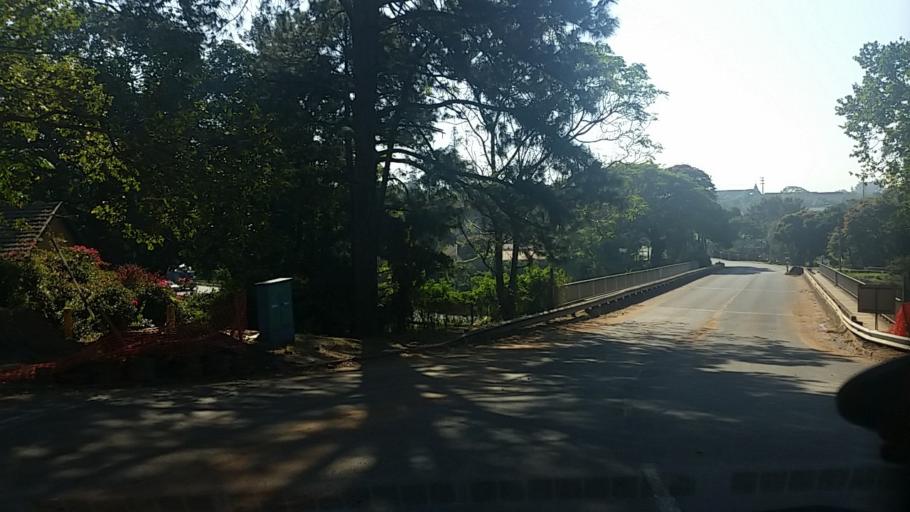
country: ZA
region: KwaZulu-Natal
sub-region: eThekwini Metropolitan Municipality
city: Berea
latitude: -29.8412
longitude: 30.9142
